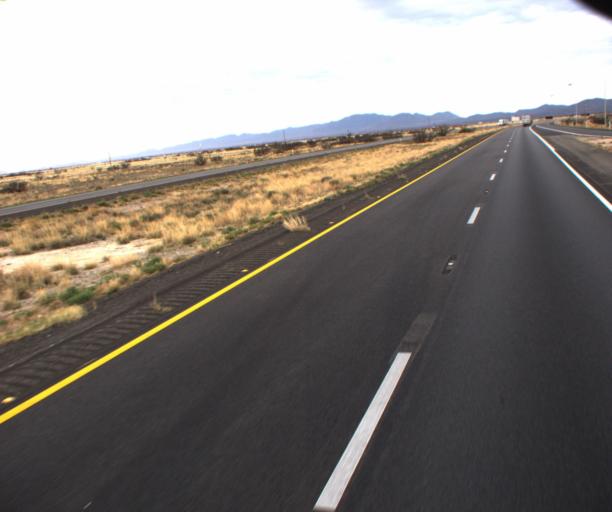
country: US
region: Arizona
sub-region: Cochise County
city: Willcox
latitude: 32.2198
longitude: -109.8804
